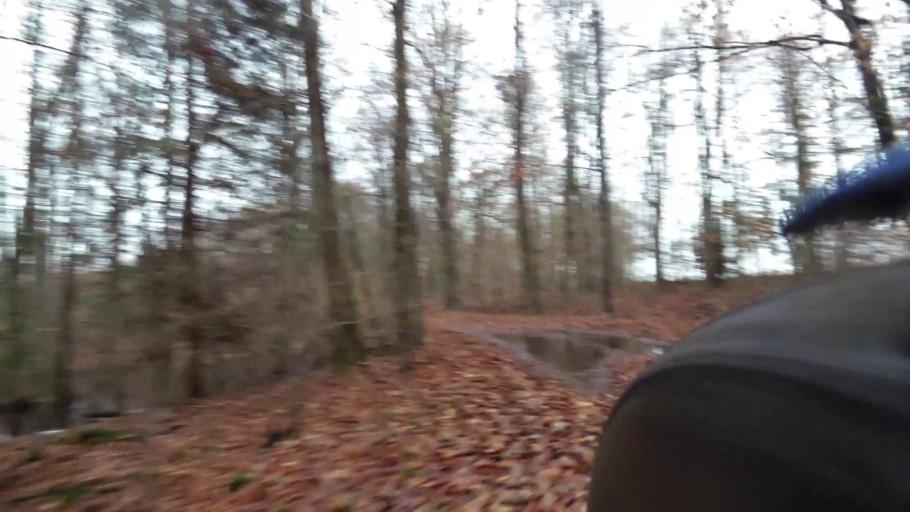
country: PL
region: West Pomeranian Voivodeship
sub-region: Powiat szczecinecki
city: Szczecinek
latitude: 53.6706
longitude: 16.6430
